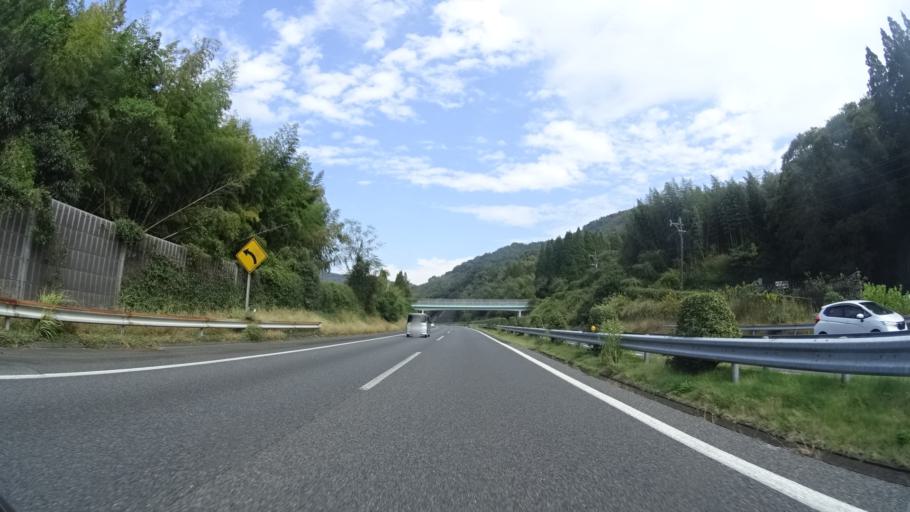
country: JP
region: Kumamoto
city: Matsubase
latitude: 32.6066
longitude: 130.7227
